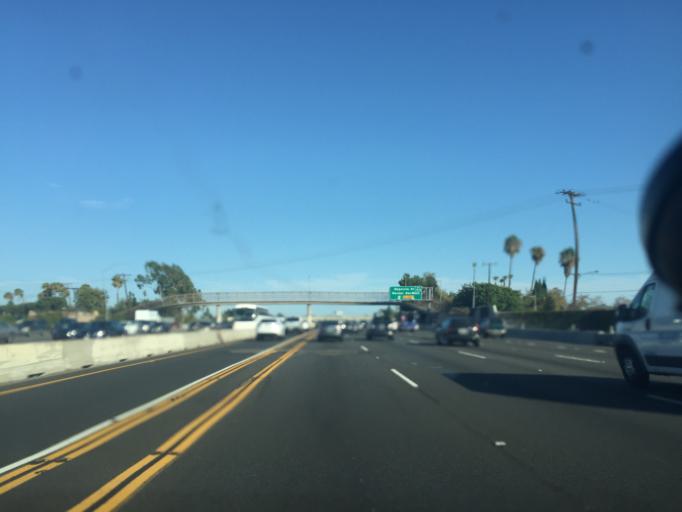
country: US
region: California
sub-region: Orange County
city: Midway City
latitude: 33.7237
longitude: -117.9766
